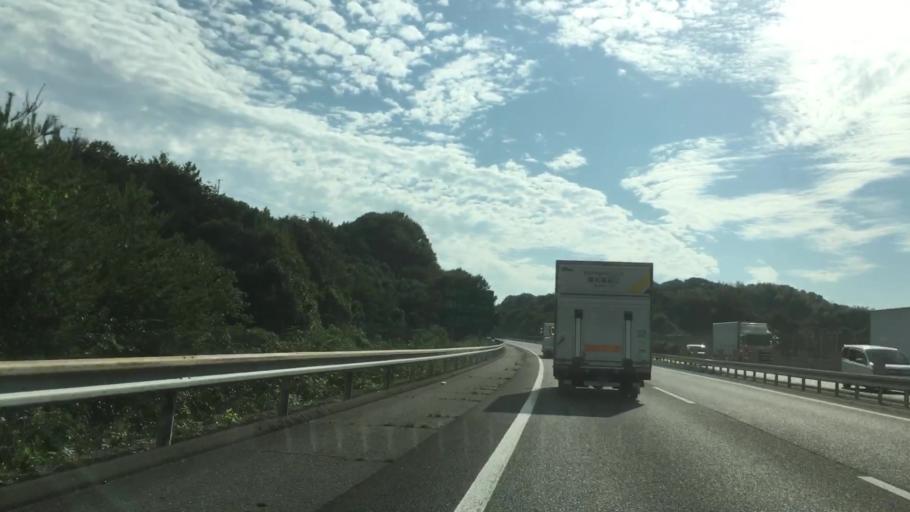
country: JP
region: Yamaguchi
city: Yanai
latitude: 34.0776
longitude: 132.0708
